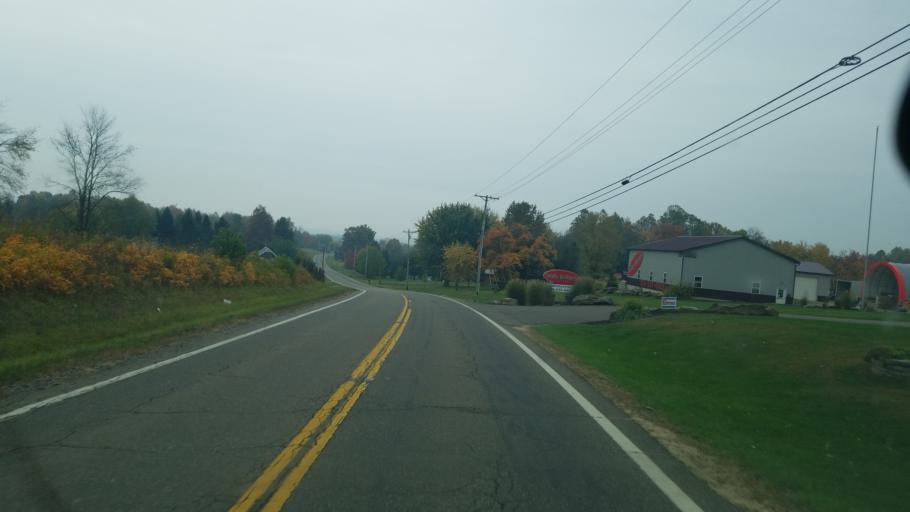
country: US
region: Ohio
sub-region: Holmes County
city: Millersburg
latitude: 40.4928
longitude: -81.8971
